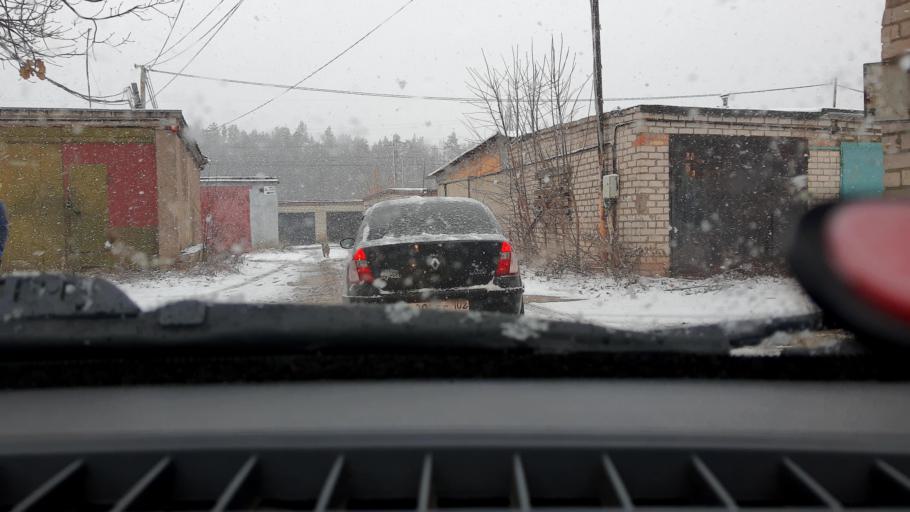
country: RU
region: Bashkortostan
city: Ufa
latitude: 54.8020
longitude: 56.0399
